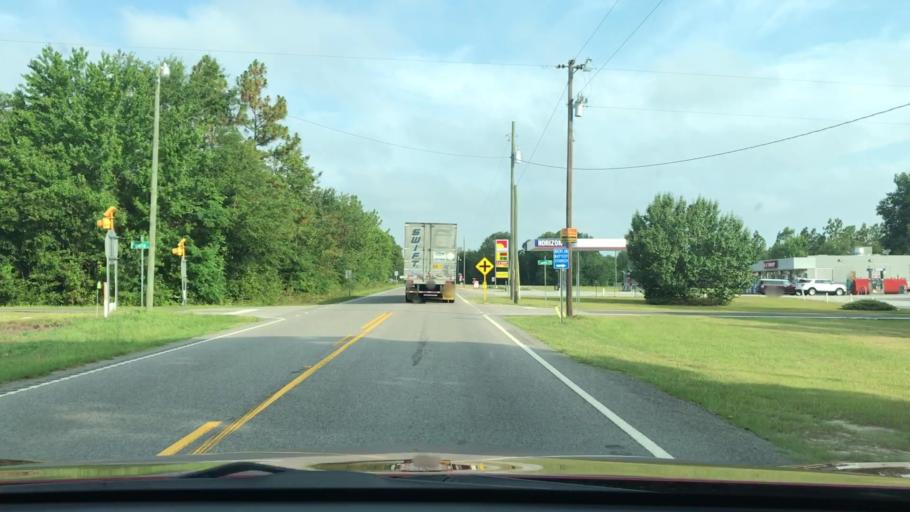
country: US
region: South Carolina
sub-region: Barnwell County
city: Williston
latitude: 33.6277
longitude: -81.3008
